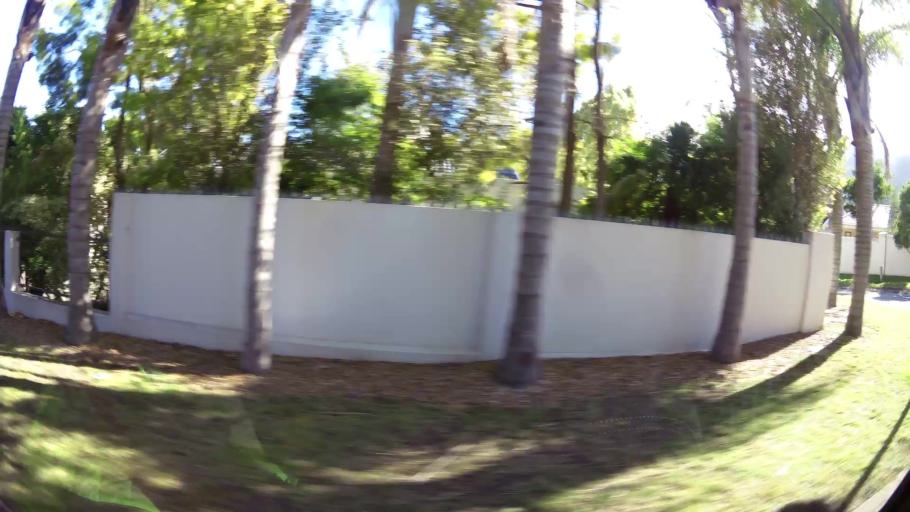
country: ZA
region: Western Cape
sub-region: Eden District Municipality
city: George
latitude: -33.9470
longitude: 22.4612
